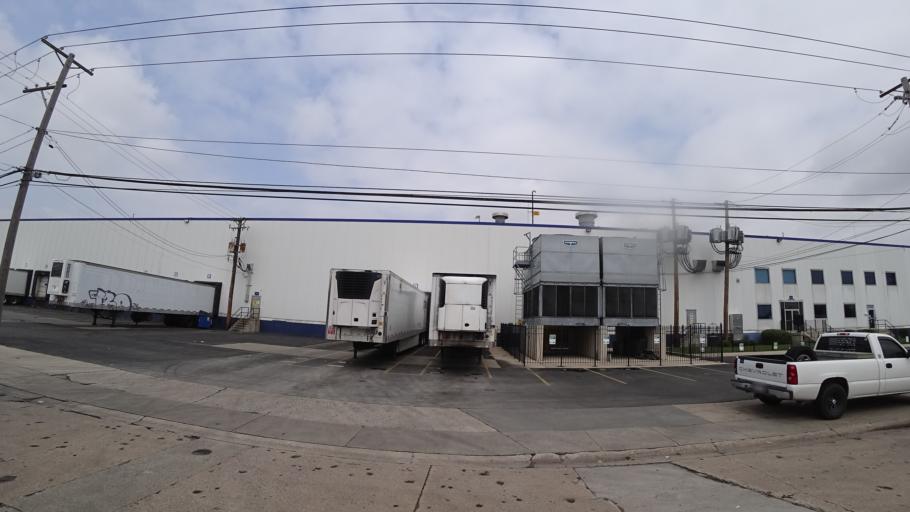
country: US
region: Illinois
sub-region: Cook County
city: Chicago
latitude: 41.8434
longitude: -87.6840
